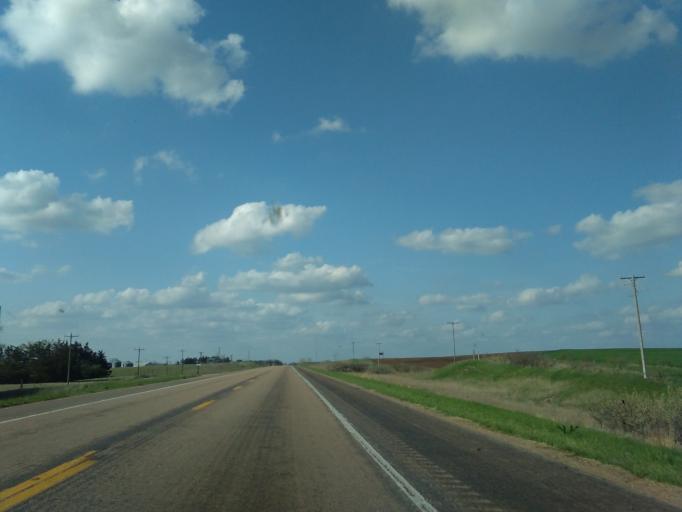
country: US
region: Nebraska
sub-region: Webster County
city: Red Cloud
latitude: 40.1426
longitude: -98.5190
